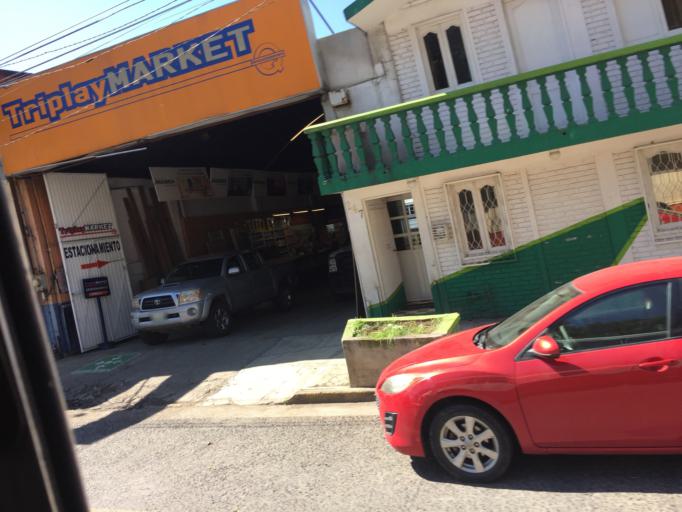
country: MX
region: Veracruz
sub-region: Xalapa
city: Xalapa de Enriquez
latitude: 19.5447
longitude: -96.9279
